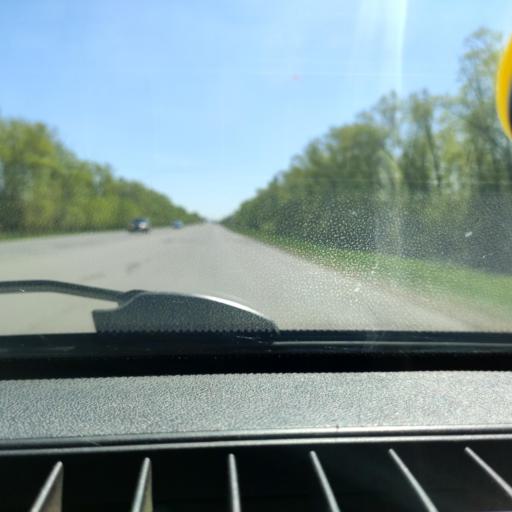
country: RU
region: Samara
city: Tol'yatti
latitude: 53.5941
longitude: 49.4072
